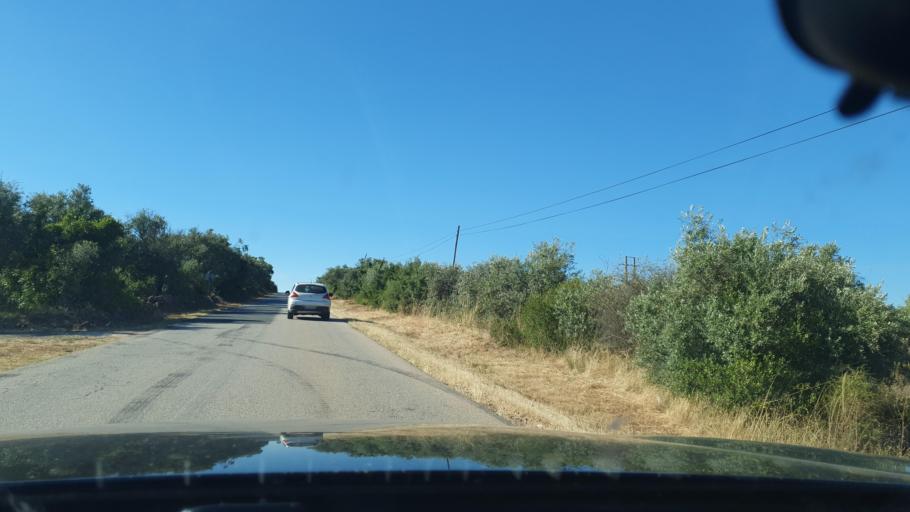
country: PT
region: Evora
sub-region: Vila Vicosa
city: Vila Vicosa
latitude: 38.7508
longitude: -7.4087
